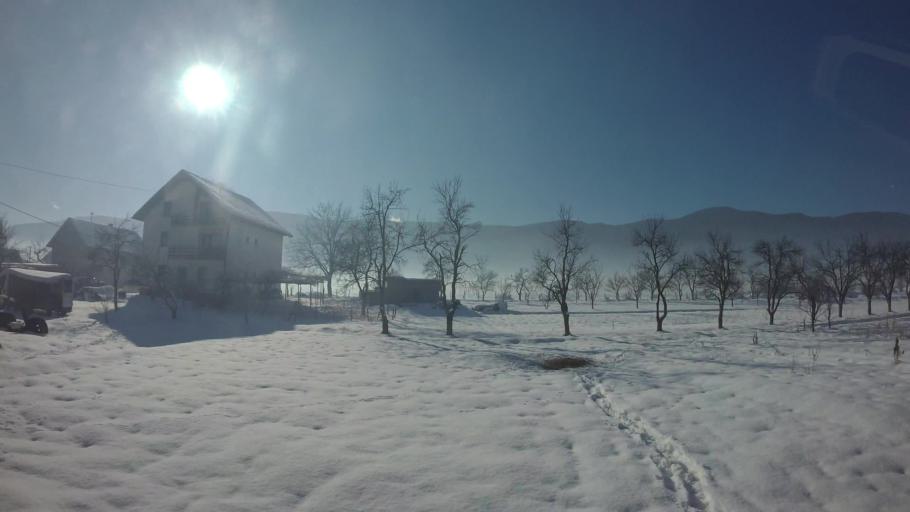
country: BA
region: Federation of Bosnia and Herzegovina
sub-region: Kanton Sarajevo
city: Sarajevo
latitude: 43.7994
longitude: 18.3356
